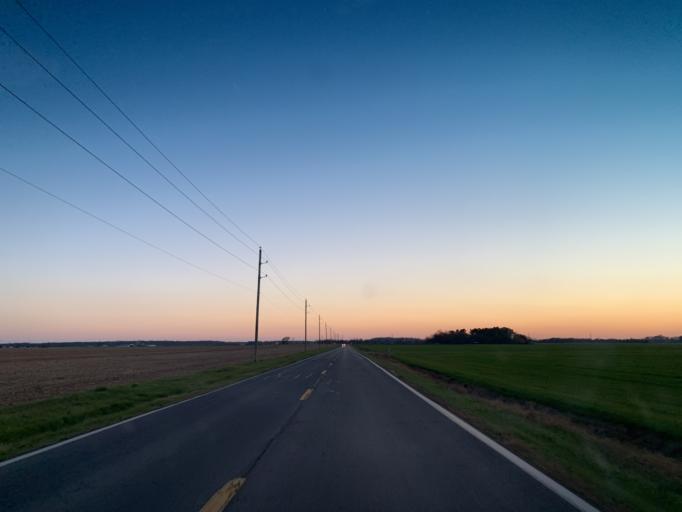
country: US
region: Delaware
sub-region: New Castle County
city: Middletown
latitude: 39.4155
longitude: -75.7456
